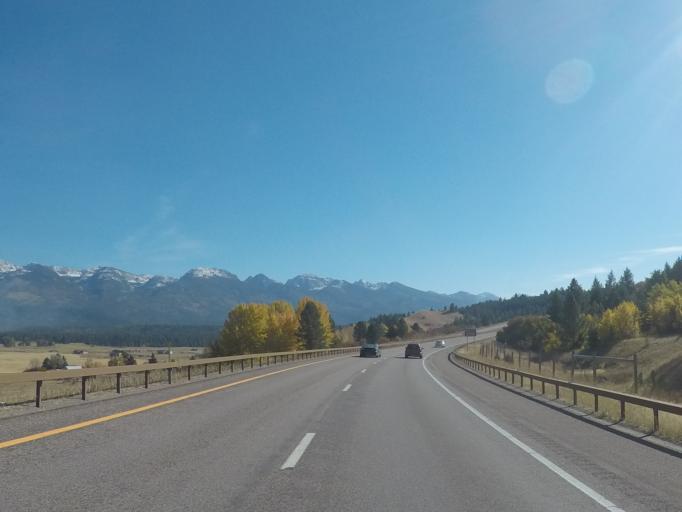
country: US
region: Montana
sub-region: Lake County
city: Polson
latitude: 47.6773
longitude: -114.1096
